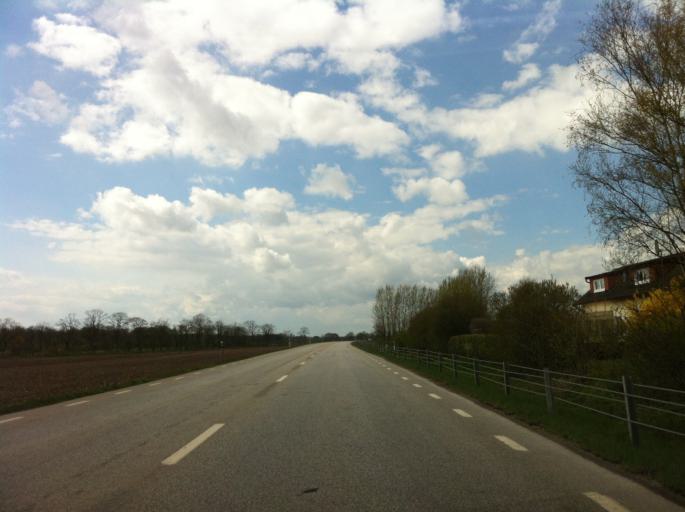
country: SE
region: Skane
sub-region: Eslovs Kommun
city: Stehag
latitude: 55.8467
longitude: 13.4453
